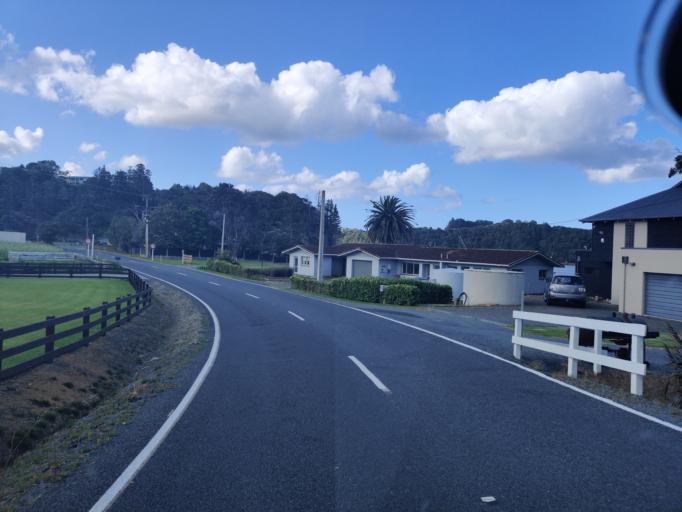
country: NZ
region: Northland
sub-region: Whangarei
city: Ngunguru
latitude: -35.6183
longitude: 174.5297
